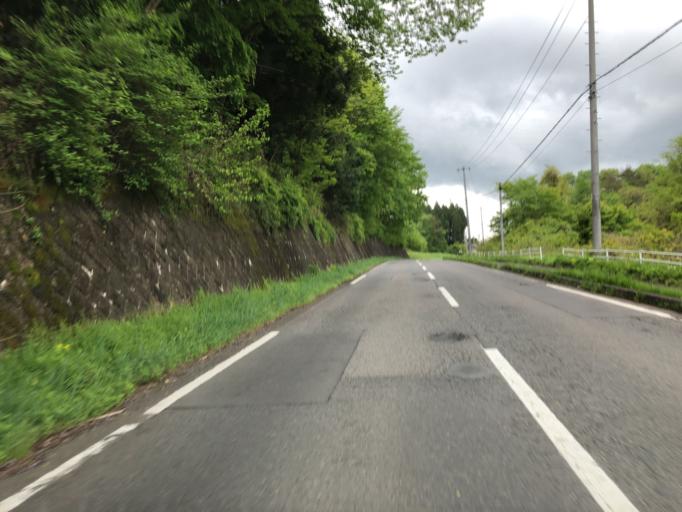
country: JP
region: Fukushima
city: Ishikawa
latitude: 37.1690
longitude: 140.4009
